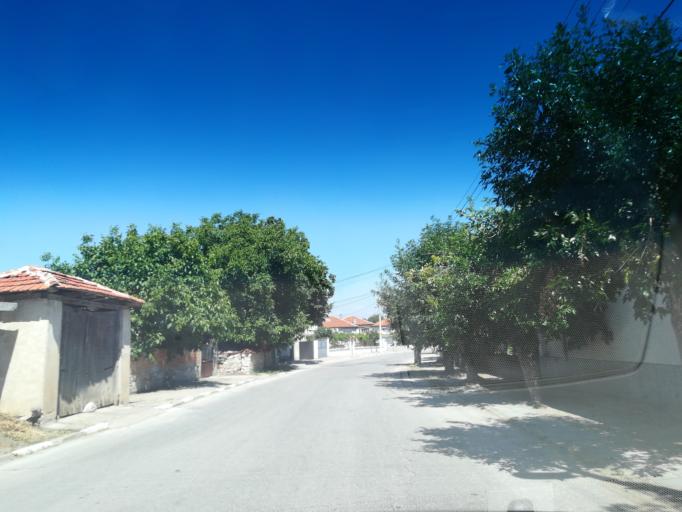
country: BG
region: Plovdiv
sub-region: Obshtina Sadovo
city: Sadovo
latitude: 42.0119
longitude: 25.0468
